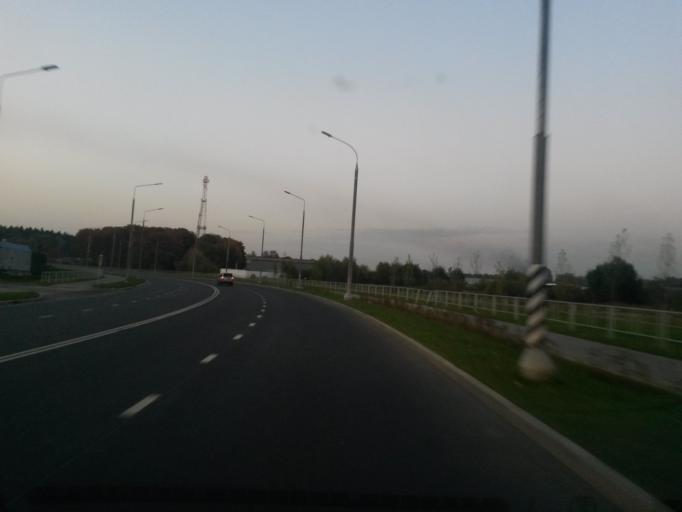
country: RU
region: Moskovskaya
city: Kommunarka
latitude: 55.5550
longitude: 37.4915
